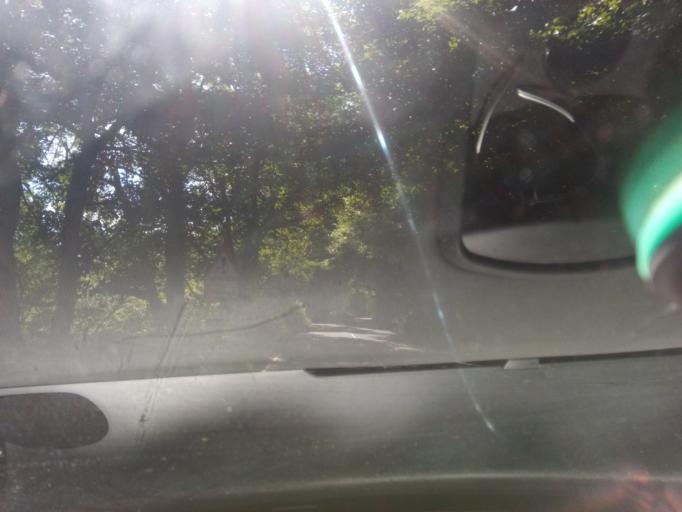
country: GB
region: England
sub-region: Northumberland
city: Bardon Mill
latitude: 54.9260
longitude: -2.3146
